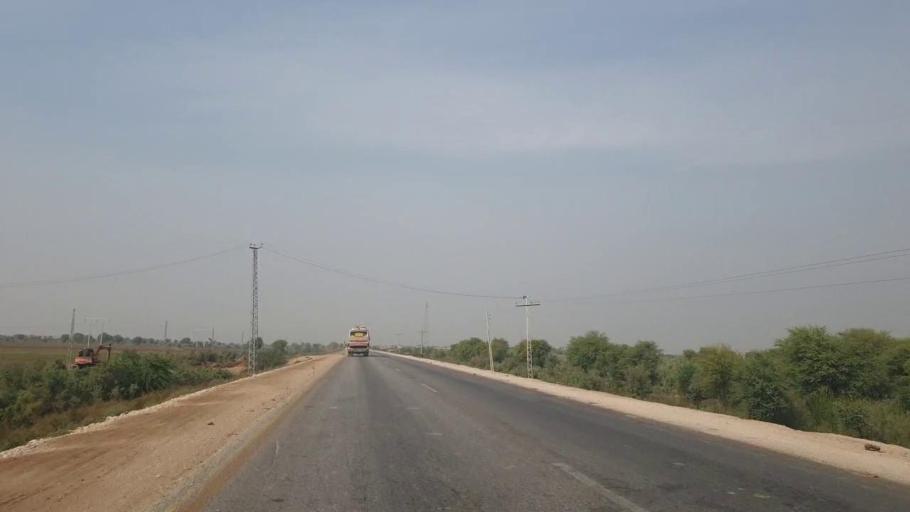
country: PK
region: Sindh
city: Sann
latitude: 26.0767
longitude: 68.0963
